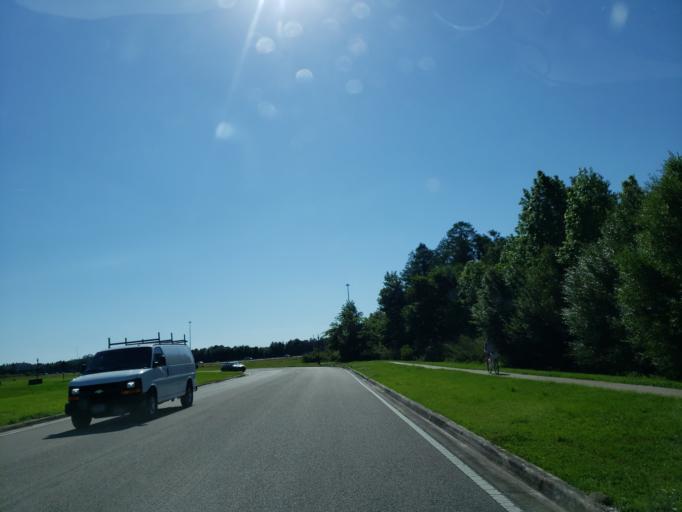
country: US
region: Florida
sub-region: Pasco County
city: Wesley Chapel
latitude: 28.2300
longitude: -82.3559
